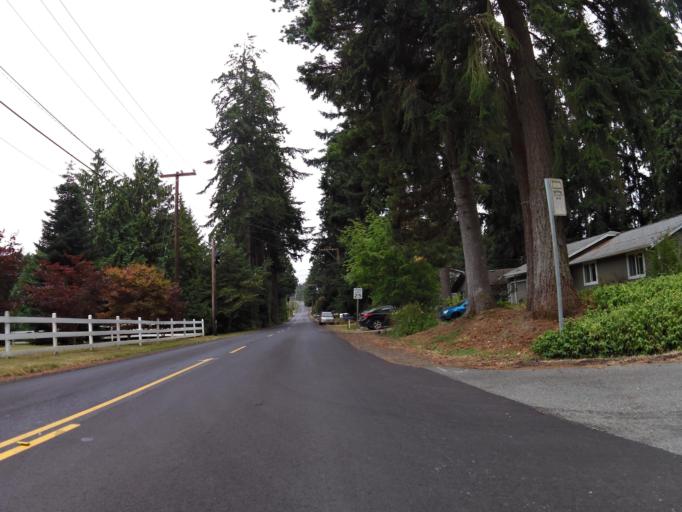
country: US
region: Washington
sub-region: Kitsap County
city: Lofall
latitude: 47.8062
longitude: -122.6600
